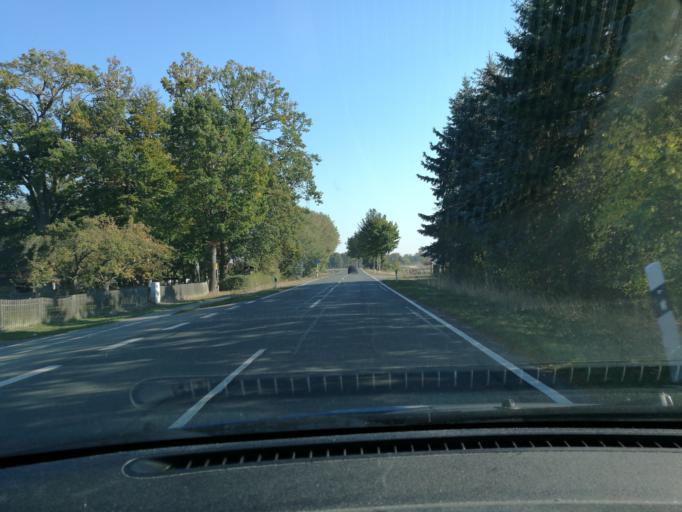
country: DE
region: Lower Saxony
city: Dannenberg
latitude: 53.0970
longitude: 11.0742
